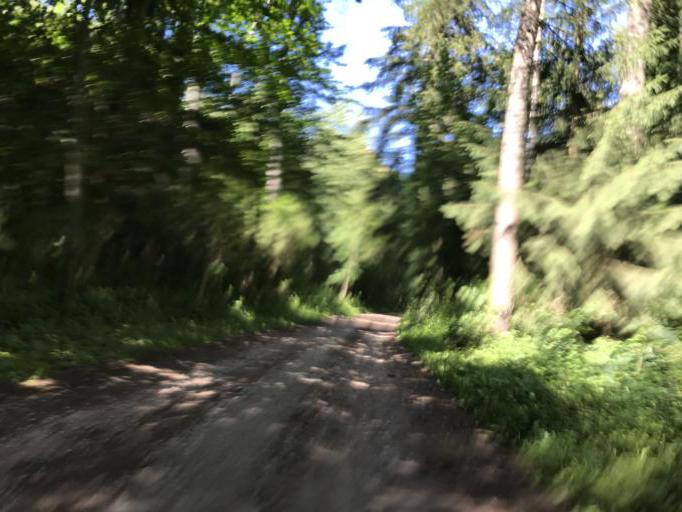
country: DE
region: Baden-Wuerttemberg
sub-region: Freiburg Region
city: Schopfheim
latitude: 47.6308
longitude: 7.8343
